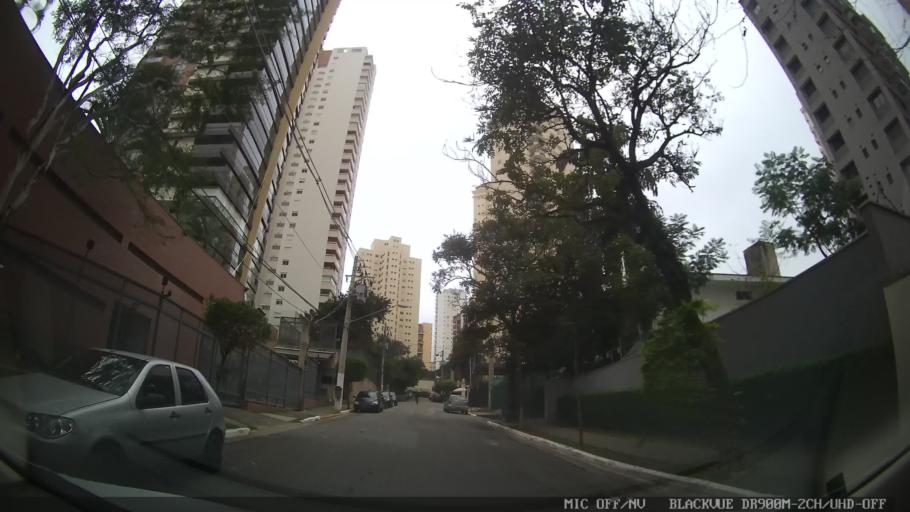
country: BR
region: Sao Paulo
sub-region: Sao Paulo
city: Sao Paulo
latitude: -23.5908
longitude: -46.6234
